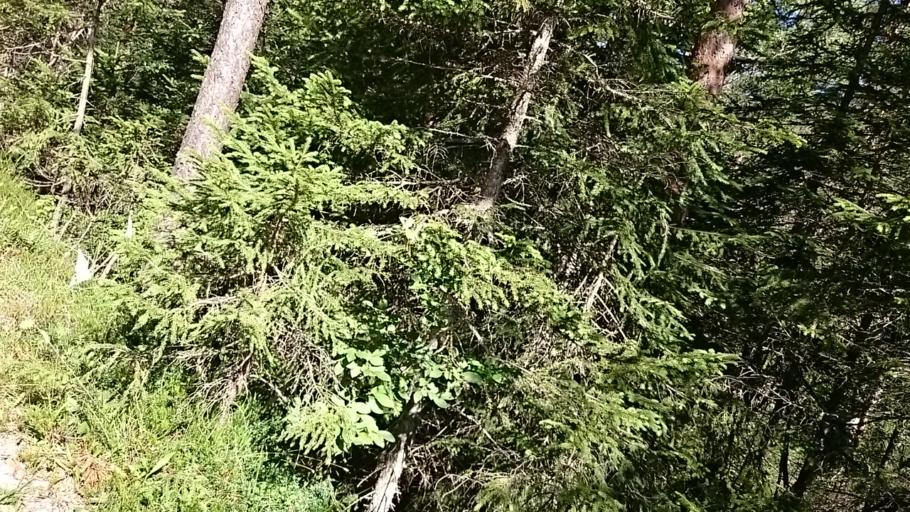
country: IT
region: Veneto
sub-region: Provincia di Belluno
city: Cortina d'Ampezzo
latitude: 46.6185
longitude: 12.2098
